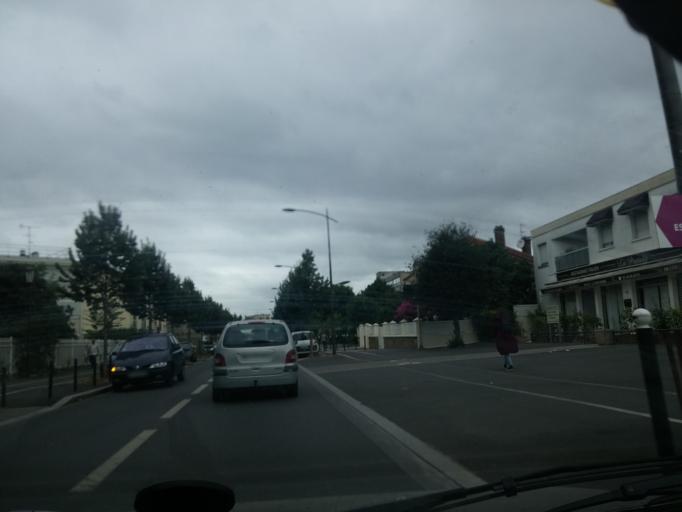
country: FR
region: Ile-de-France
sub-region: Departement du Val-de-Marne
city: Chevilly-Larue
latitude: 48.7682
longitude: 2.3723
